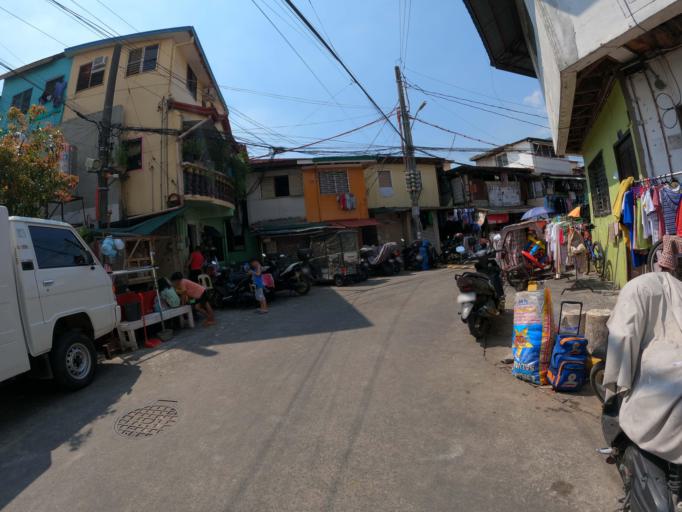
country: PH
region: Metro Manila
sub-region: San Juan
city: San Juan
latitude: 14.5914
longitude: 121.0179
